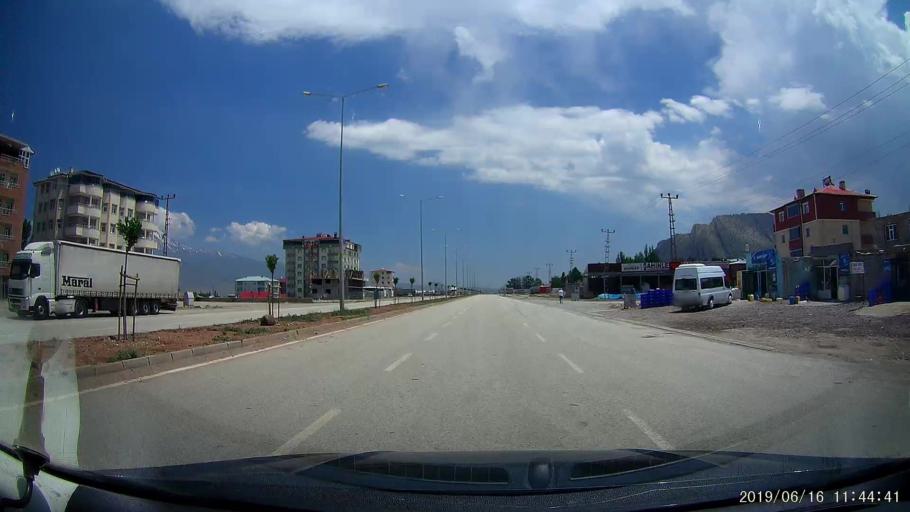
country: TR
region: Agri
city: Dogubayazit
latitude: 39.5573
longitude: 44.0920
